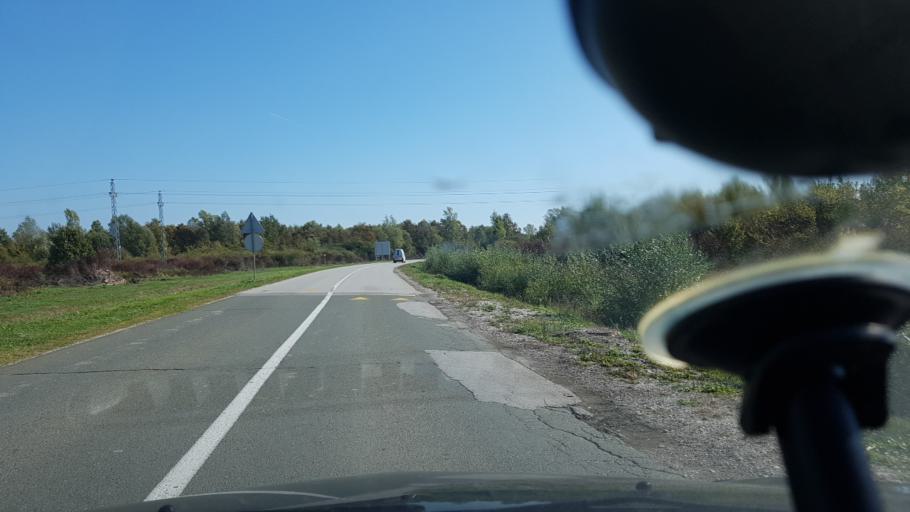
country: HR
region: Zagrebacka
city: Brckovljani
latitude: 45.7662
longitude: 16.2349
